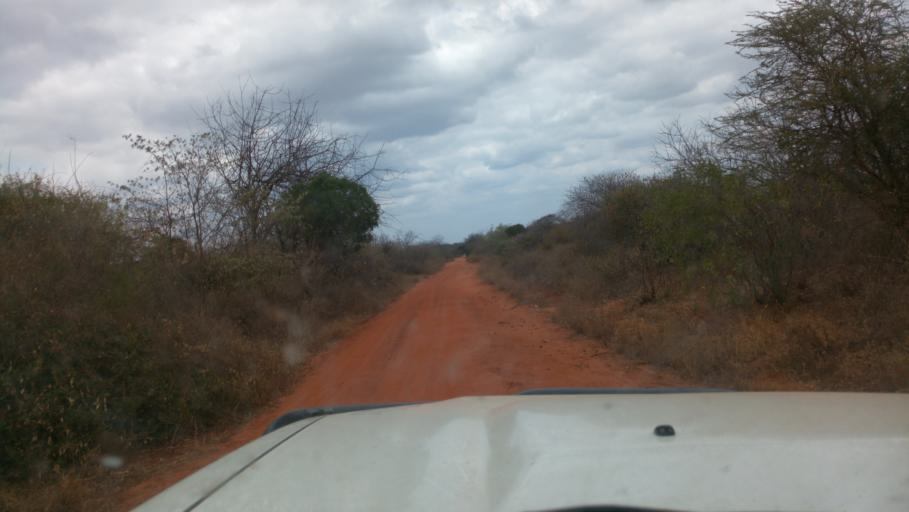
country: KE
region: Kitui
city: Kitui
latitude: -1.8876
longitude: 38.4000
